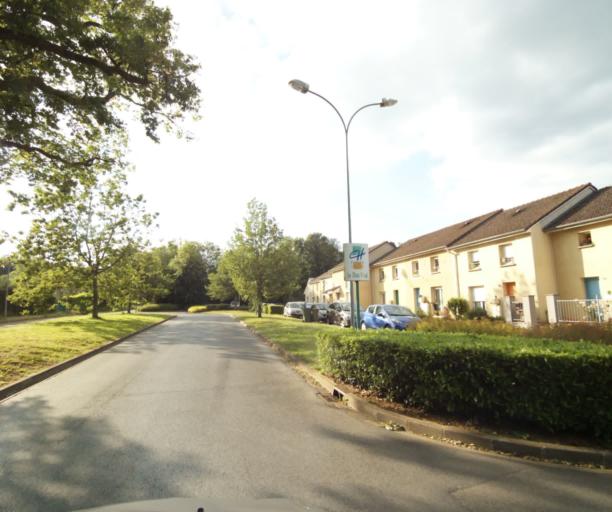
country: FR
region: Champagne-Ardenne
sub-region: Departement des Ardennes
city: Charleville-Mezieres
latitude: 49.7927
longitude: 4.7221
